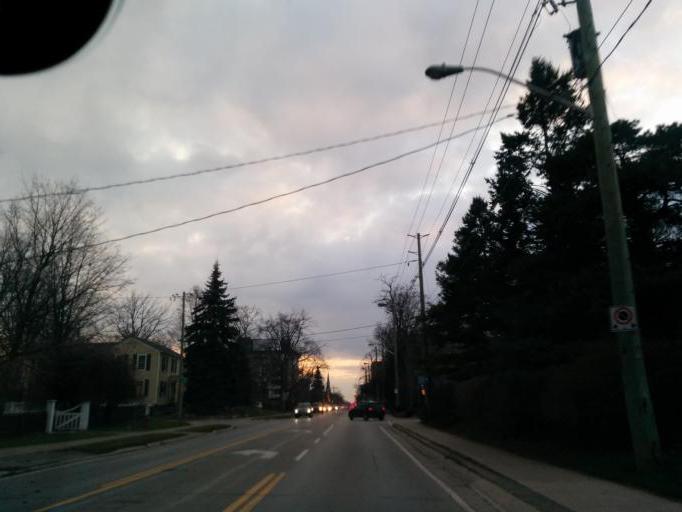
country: CA
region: Ontario
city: Oakville
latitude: 43.4510
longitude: -79.6627
